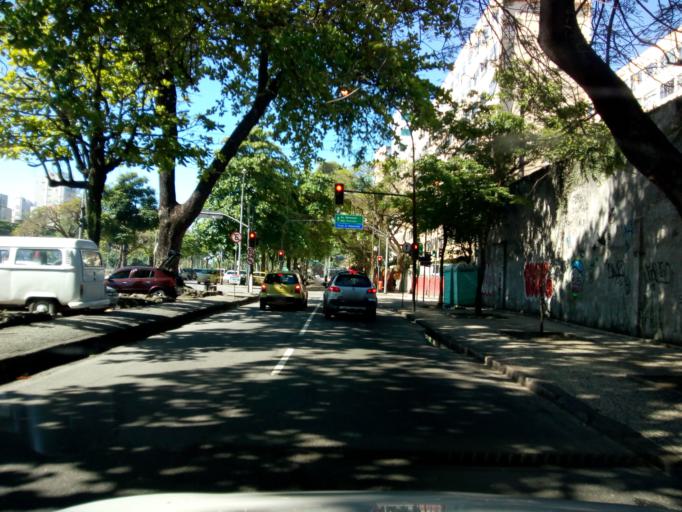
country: BR
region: Rio de Janeiro
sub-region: Rio De Janeiro
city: Rio de Janeiro
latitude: -22.9813
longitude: -43.2150
